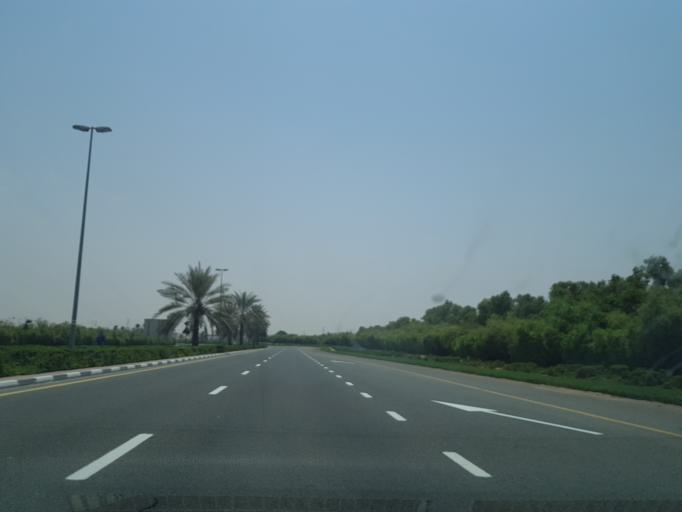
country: AE
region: Ash Shariqah
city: Sharjah
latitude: 25.1119
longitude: 55.3946
